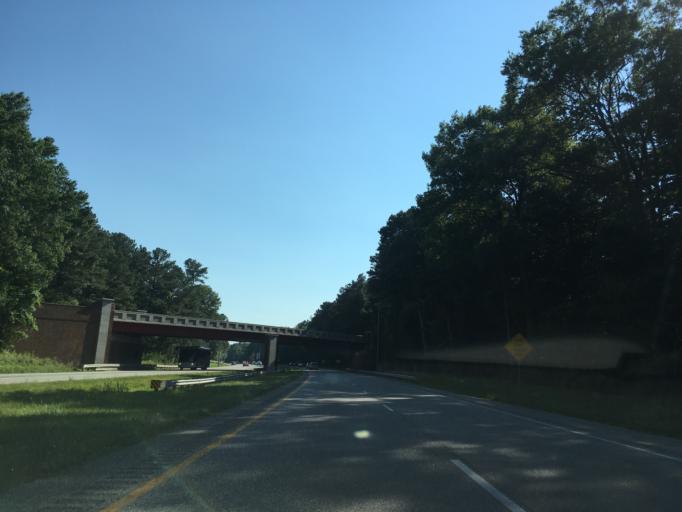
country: US
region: Maryland
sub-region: Queen Anne's County
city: Grasonville
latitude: 38.9821
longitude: -76.1670
